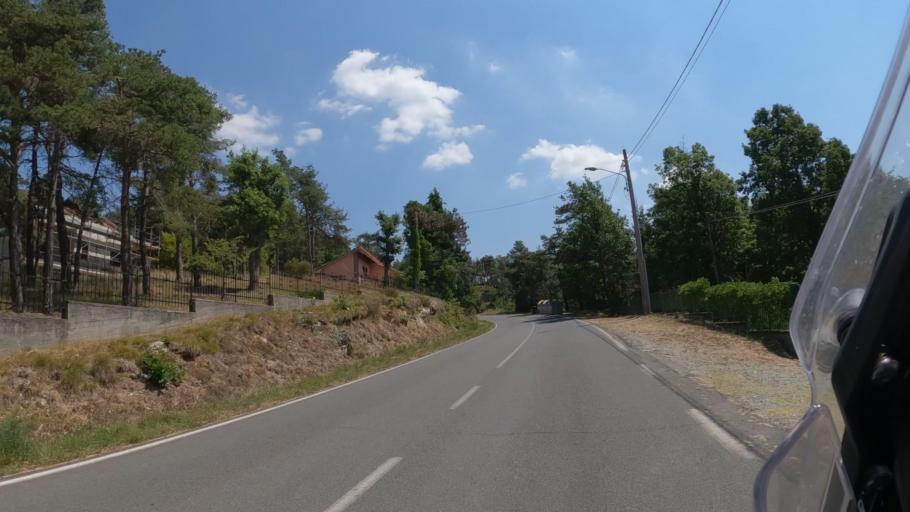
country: IT
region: Piedmont
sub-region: Provincia di Alessandria
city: Morbello
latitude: 44.5552
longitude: 8.4993
